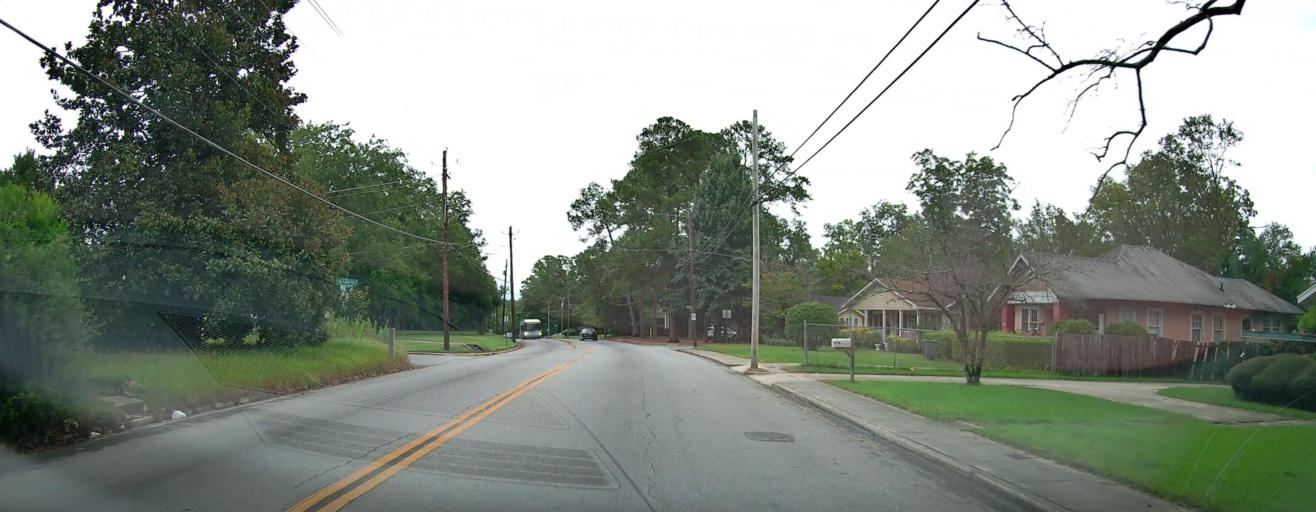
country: US
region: Georgia
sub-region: Bibb County
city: Macon
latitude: 32.8408
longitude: -83.6852
